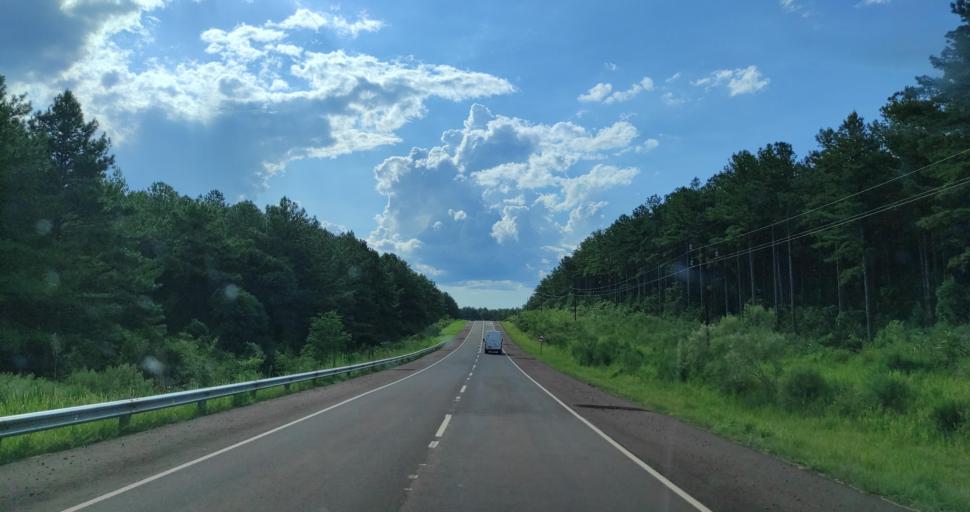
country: AR
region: Misiones
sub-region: Departamento de San Pedro
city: San Pedro
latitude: -26.3505
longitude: -53.9664
